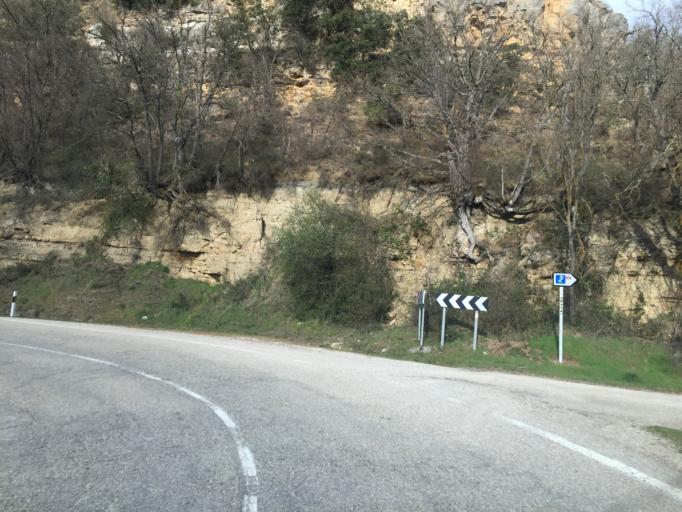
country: ES
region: Castille and Leon
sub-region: Provincia de Burgos
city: Tubilla del Agua
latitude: 42.8014
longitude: -3.7685
